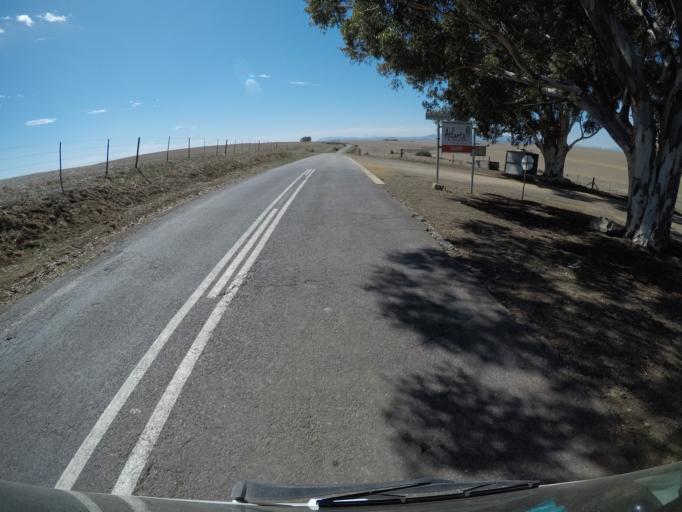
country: ZA
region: Western Cape
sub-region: City of Cape Town
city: Atlantis
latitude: -33.6984
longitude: 18.5896
